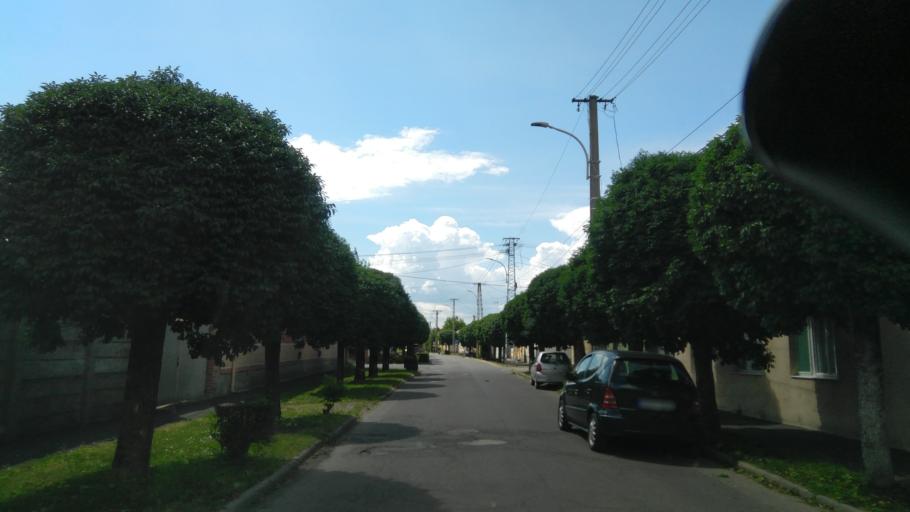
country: HU
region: Bekes
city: Gyula
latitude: 46.6468
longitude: 21.2639
